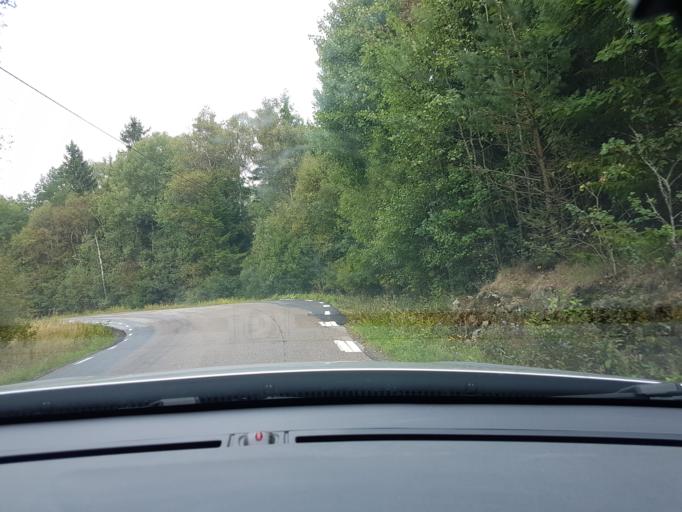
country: SE
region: Vaestra Goetaland
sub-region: Ale Kommun
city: Skepplanda
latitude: 57.8980
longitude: 12.1939
